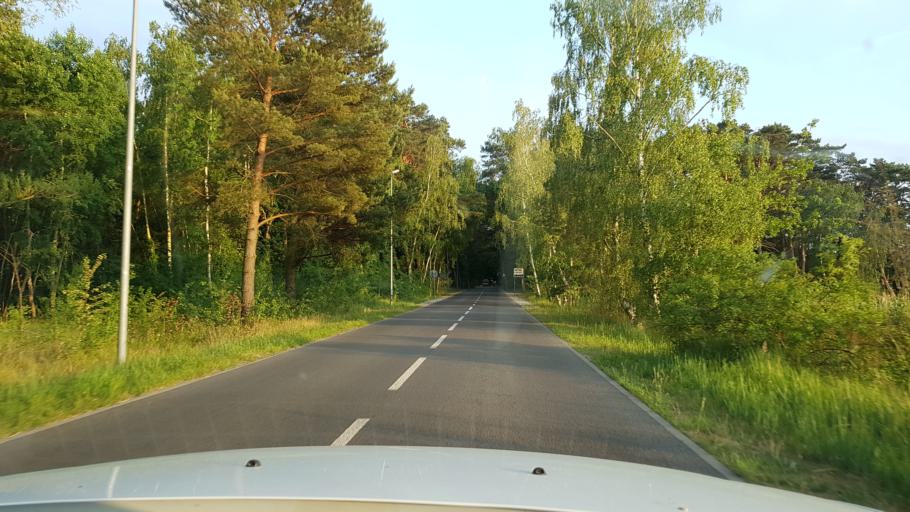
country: PL
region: West Pomeranian Voivodeship
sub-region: Swinoujscie
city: Swinoujscie
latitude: 53.8546
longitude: 14.2859
